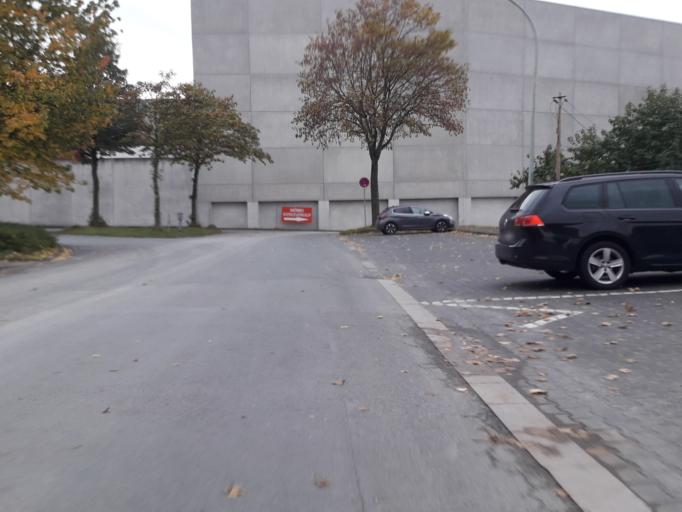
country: DE
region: North Rhine-Westphalia
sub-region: Regierungsbezirk Detmold
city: Paderborn
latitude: 51.6910
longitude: 8.7421
